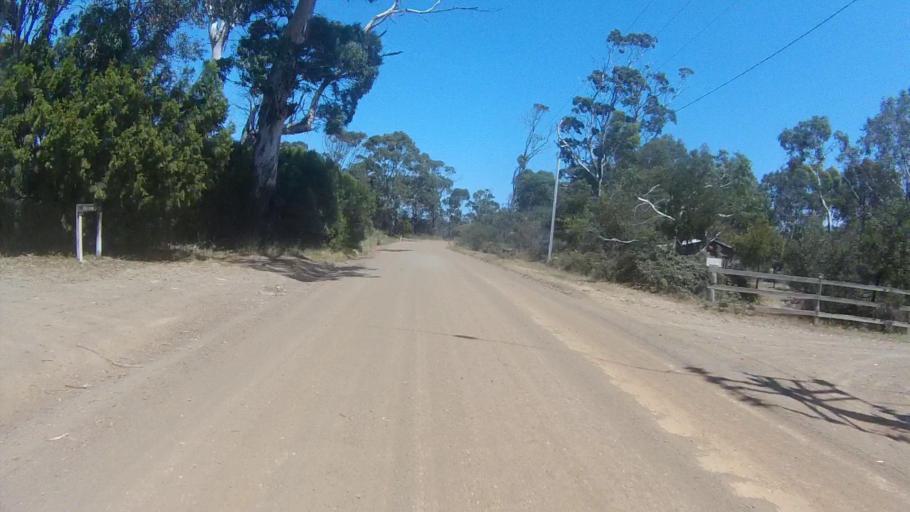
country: AU
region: Tasmania
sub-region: Sorell
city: Sorell
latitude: -42.8355
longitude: 147.8547
